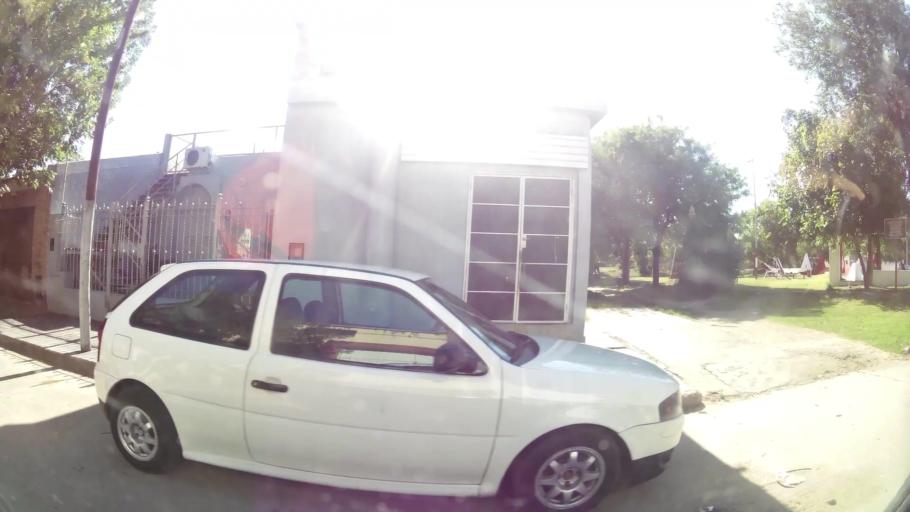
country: AR
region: Cordoba
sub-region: Departamento de Capital
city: Cordoba
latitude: -31.3786
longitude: -64.1894
